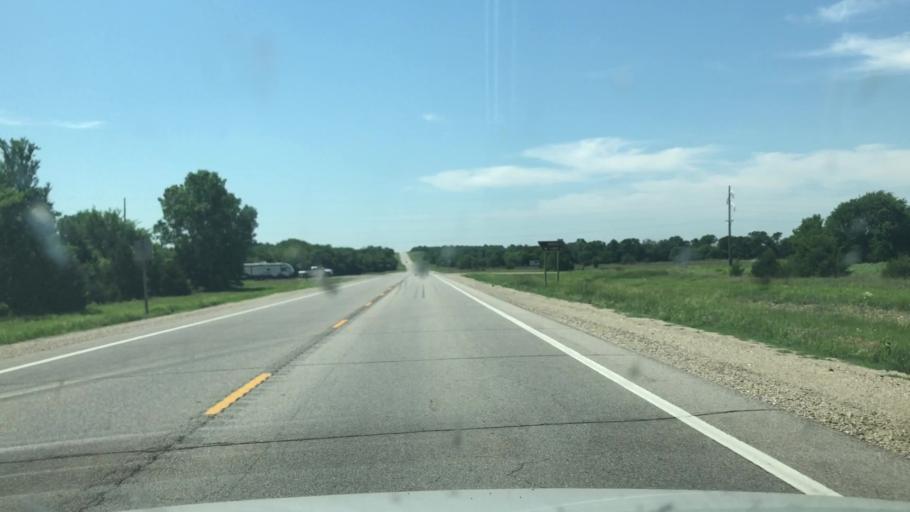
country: US
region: Kansas
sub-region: Cowley County
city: Winfield
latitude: 37.3623
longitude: -97.0073
